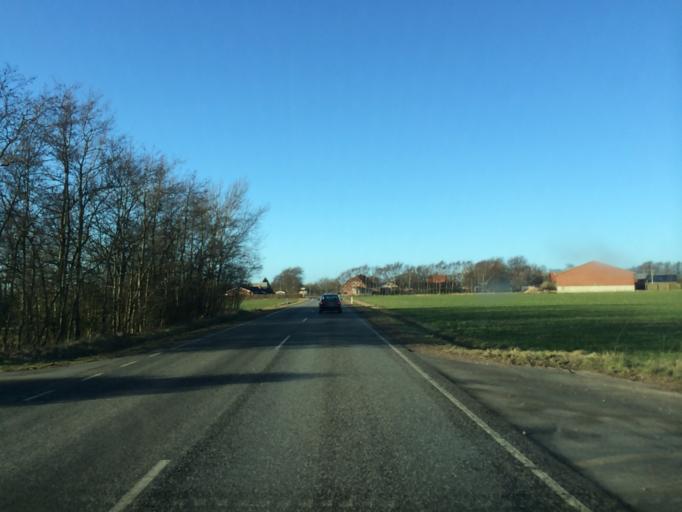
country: DK
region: Central Jutland
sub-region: Ringkobing-Skjern Kommune
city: Ringkobing
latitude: 56.1082
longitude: 8.3209
